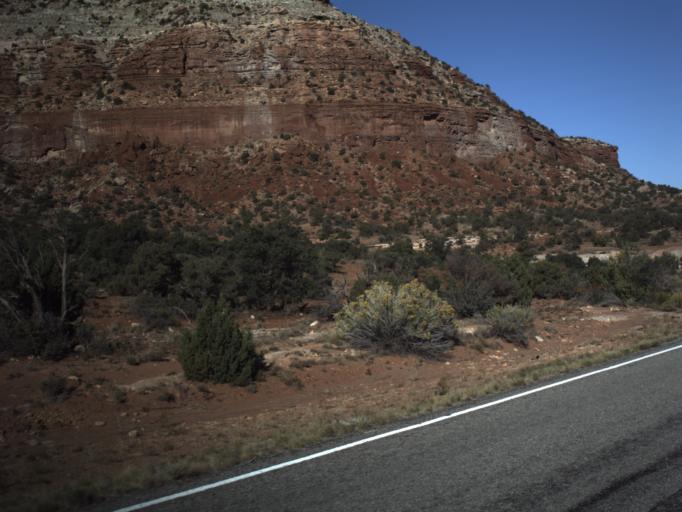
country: US
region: Utah
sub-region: San Juan County
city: Blanding
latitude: 37.6410
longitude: -110.1099
